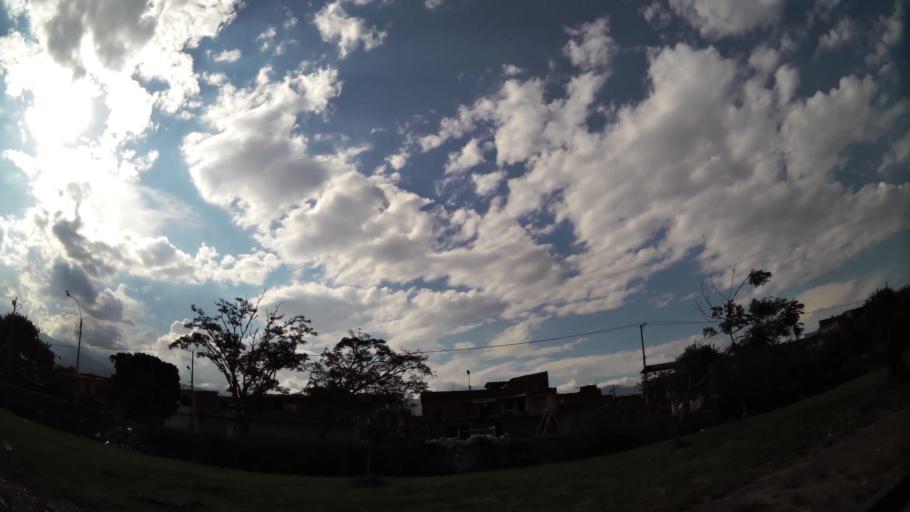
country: CO
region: Valle del Cauca
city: Cali
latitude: 3.4140
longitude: -76.4975
